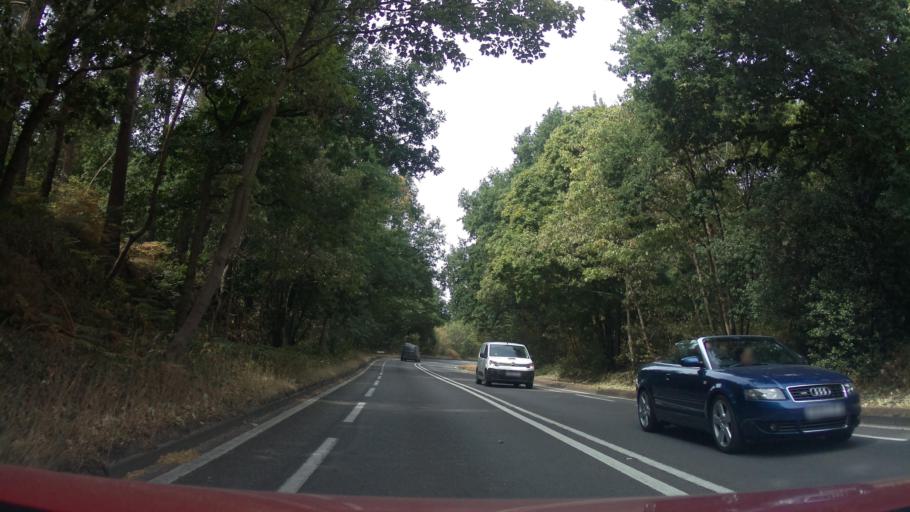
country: GB
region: England
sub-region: Surrey
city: Reigate
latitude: 51.2409
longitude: -0.2279
